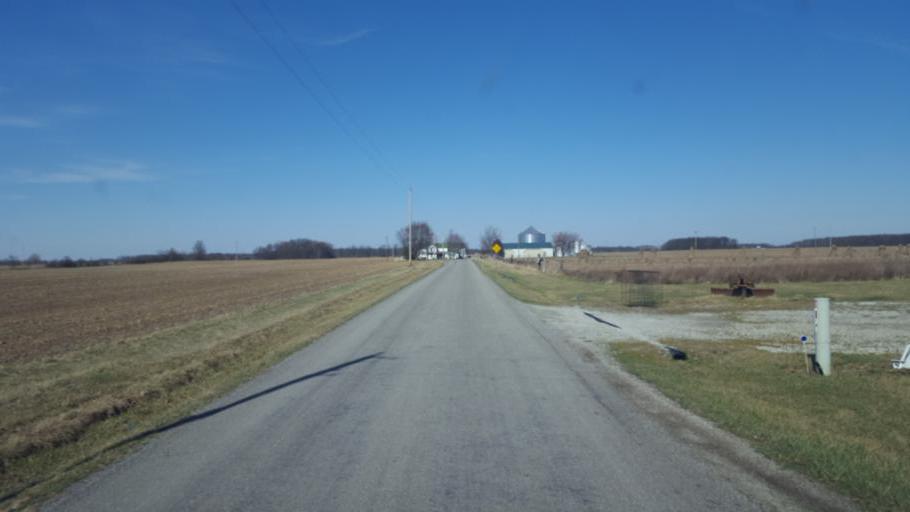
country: US
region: Ohio
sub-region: Hardin County
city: Kenton
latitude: 40.5387
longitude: -83.4566
